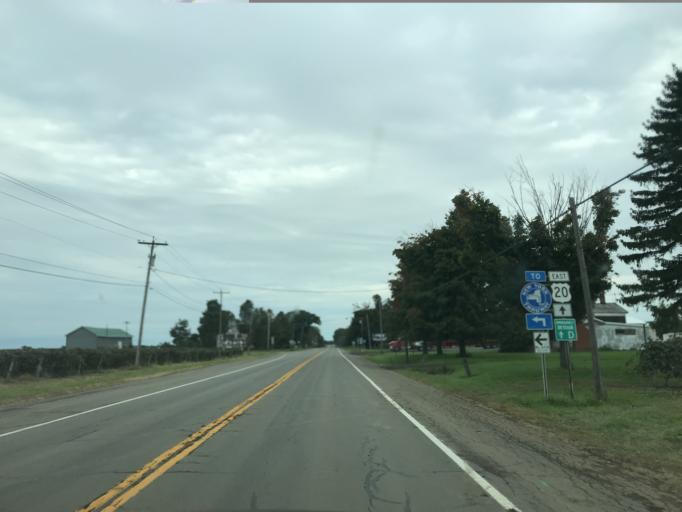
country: US
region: Pennsylvania
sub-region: Erie County
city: North East
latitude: 42.2539
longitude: -79.7405
